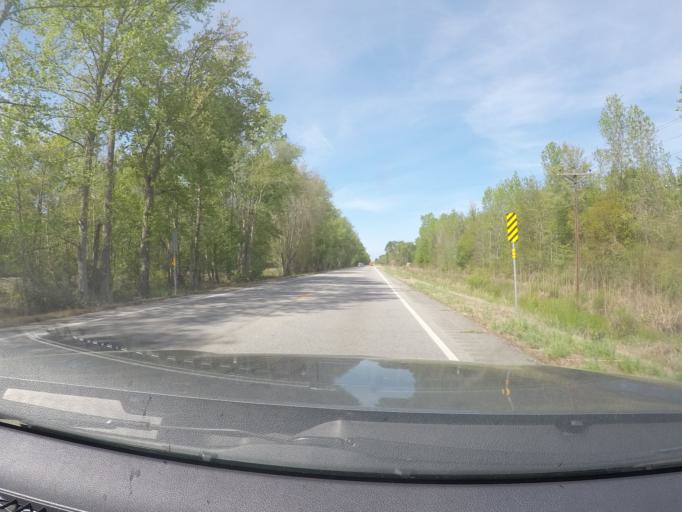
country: US
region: Georgia
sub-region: Bryan County
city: Pembroke
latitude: 32.1339
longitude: -81.5947
